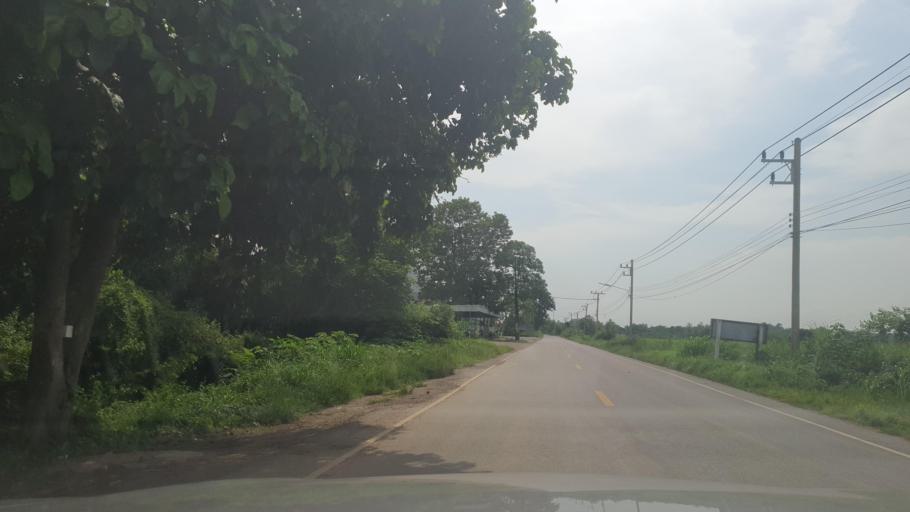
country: TH
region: Sukhothai
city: Si Samrong
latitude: 17.1199
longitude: 99.8620
